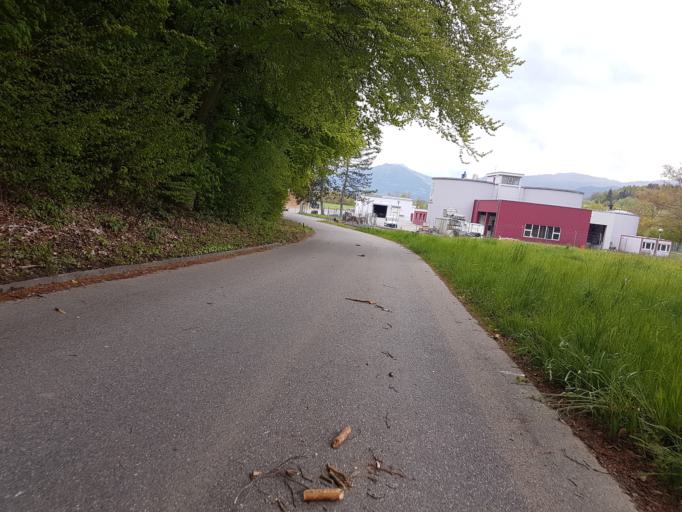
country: CH
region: Bern
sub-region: Oberaargau
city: Oberbipp
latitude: 47.2356
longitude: 7.6753
